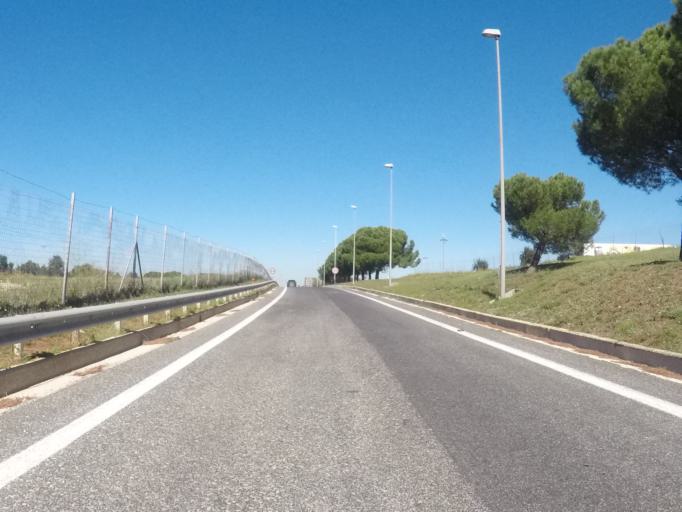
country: IT
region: Latium
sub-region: Citta metropolitana di Roma Capitale
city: Valle Martella
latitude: 41.8887
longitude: 12.7607
